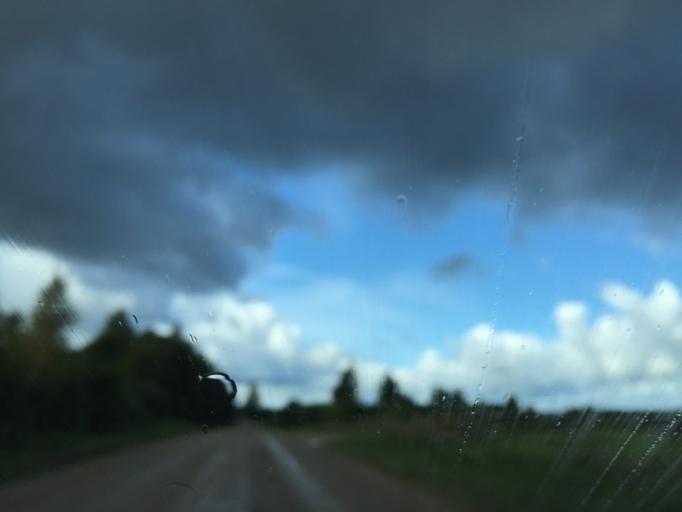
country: LV
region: Talsu Rajons
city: Sabile
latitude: 57.0509
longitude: 22.4530
